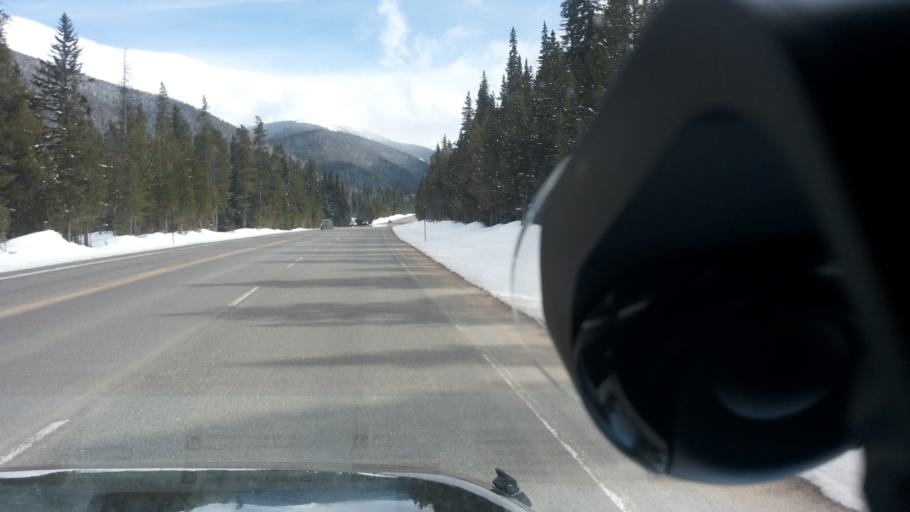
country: US
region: Colorado
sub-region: Grand County
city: Fraser
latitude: 39.8729
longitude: -105.7510
